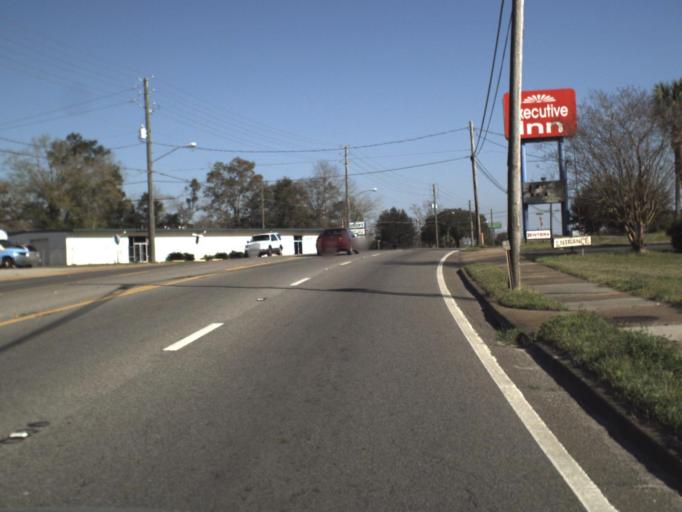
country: US
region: Florida
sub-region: Jackson County
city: Marianna
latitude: 30.7862
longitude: -85.2536
